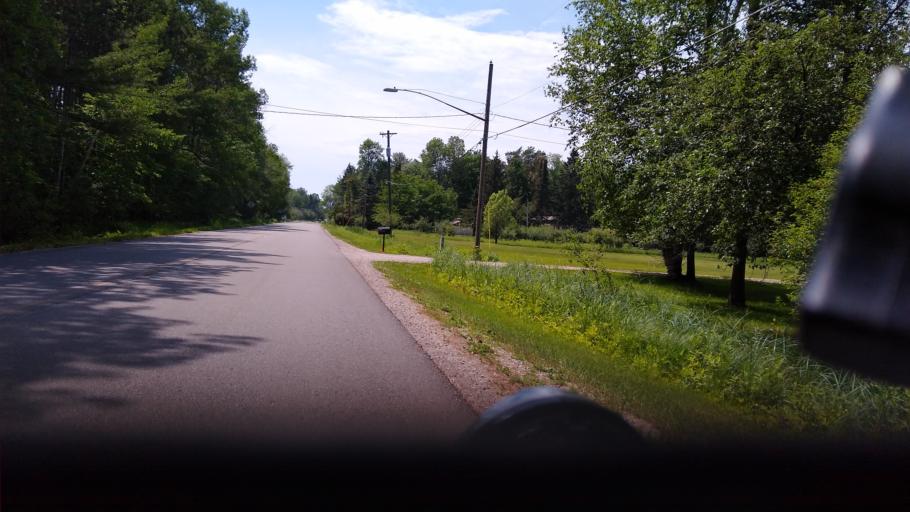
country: US
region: Michigan
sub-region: Delta County
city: Escanaba
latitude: 45.7101
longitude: -87.0968
